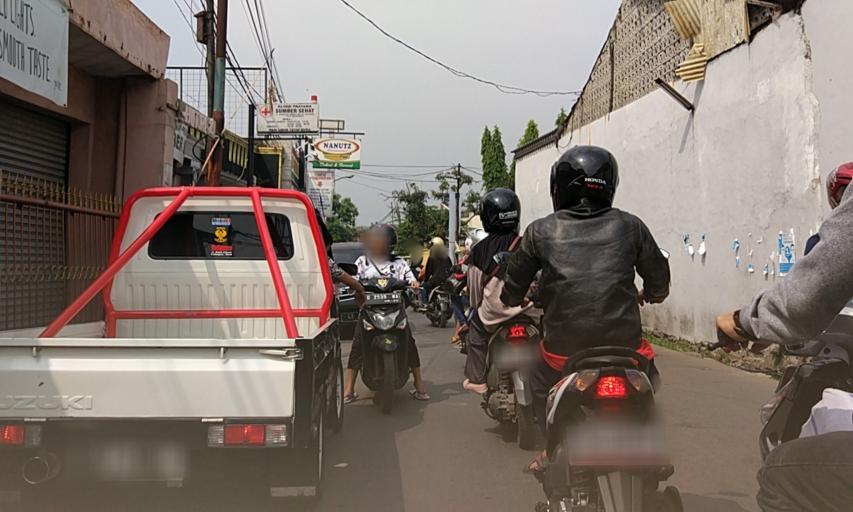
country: ID
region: West Java
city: Margahayukencana
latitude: -6.9392
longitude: 107.5829
